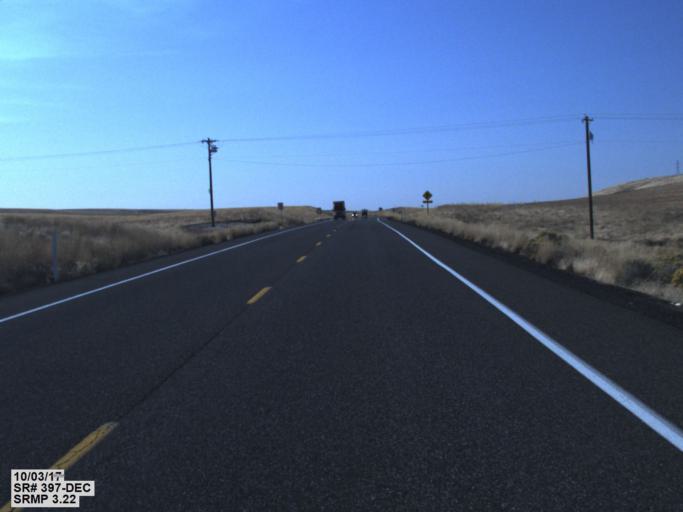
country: US
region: Washington
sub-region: Benton County
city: Highland
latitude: 46.1528
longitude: -119.1408
